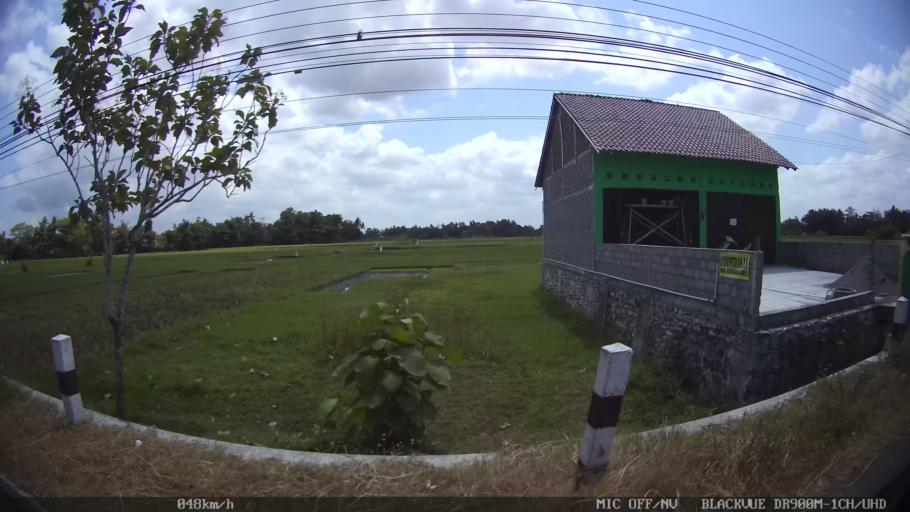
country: ID
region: Daerah Istimewa Yogyakarta
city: Bantul
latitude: -7.9045
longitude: 110.3302
